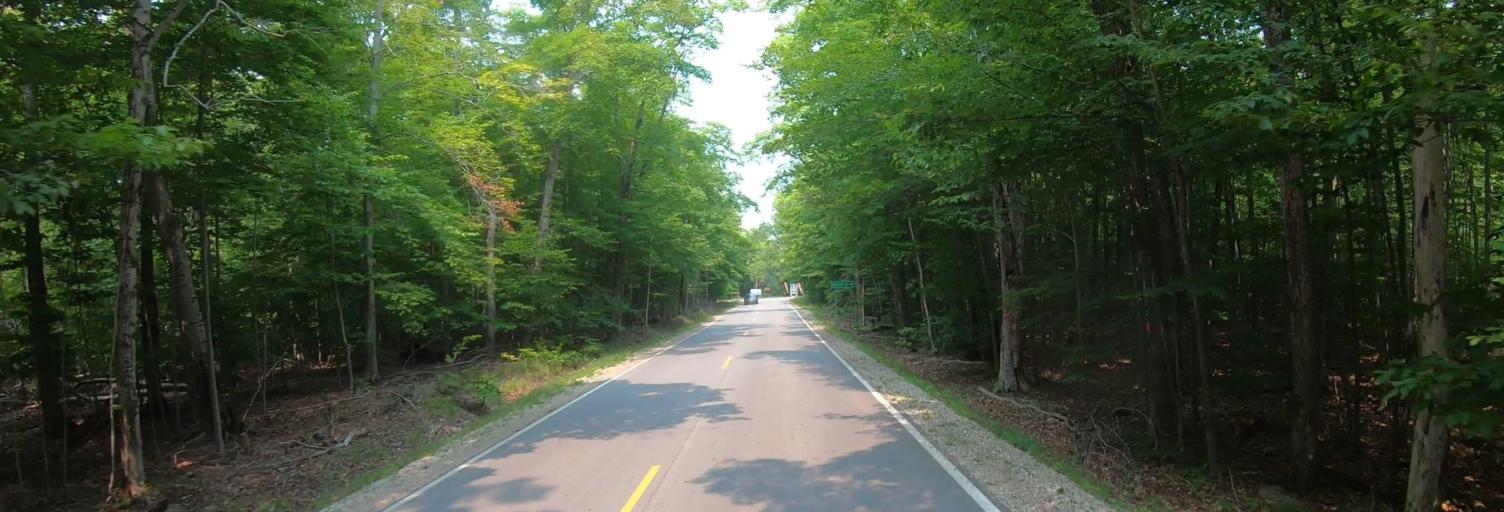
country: CA
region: Ontario
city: Thessalon
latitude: 46.0116
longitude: -83.6977
